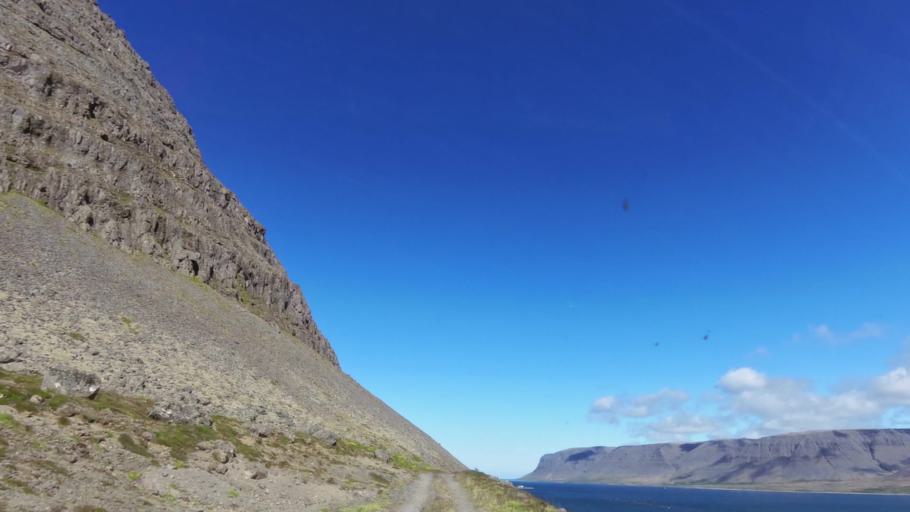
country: IS
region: West
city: Olafsvik
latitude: 65.6263
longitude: -23.9000
